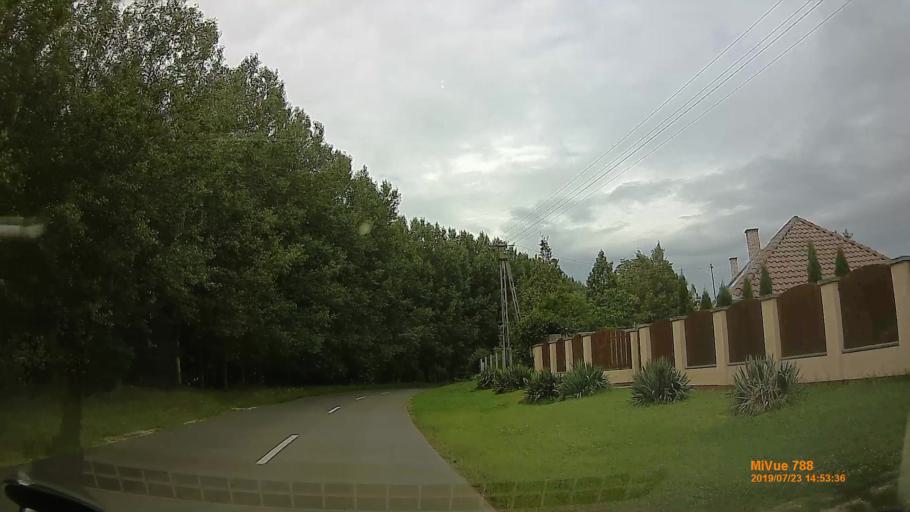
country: HU
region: Szabolcs-Szatmar-Bereg
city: Kalmanhaza
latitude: 47.8797
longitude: 21.6521
